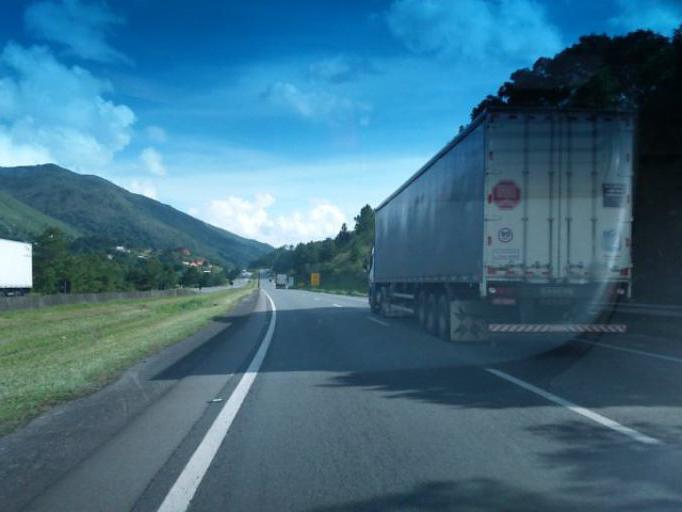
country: BR
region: Parana
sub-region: Campina Grande Do Sul
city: Campina Grande do Sul
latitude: -25.1279
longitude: -48.8575
